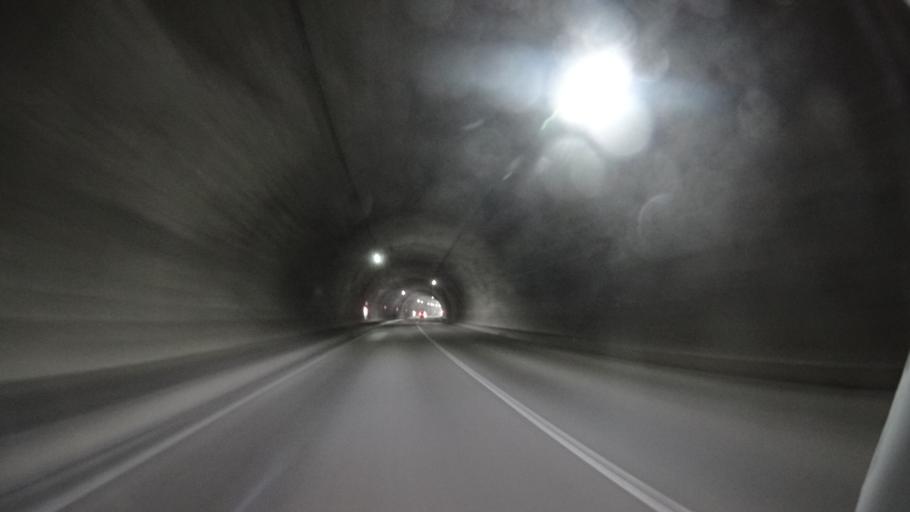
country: JP
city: Asahi
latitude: 35.9760
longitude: 135.9626
